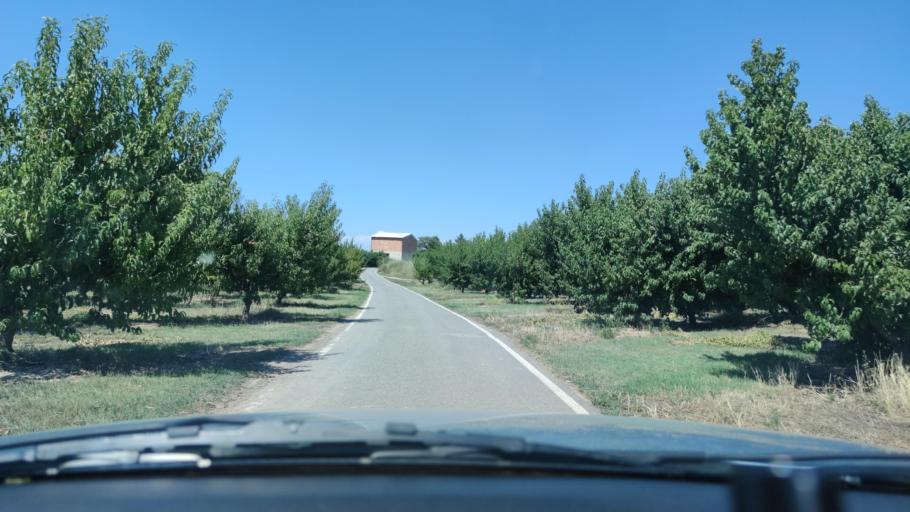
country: ES
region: Catalonia
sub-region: Provincia de Lleida
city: Corbins
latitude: 41.6754
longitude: 0.6564
